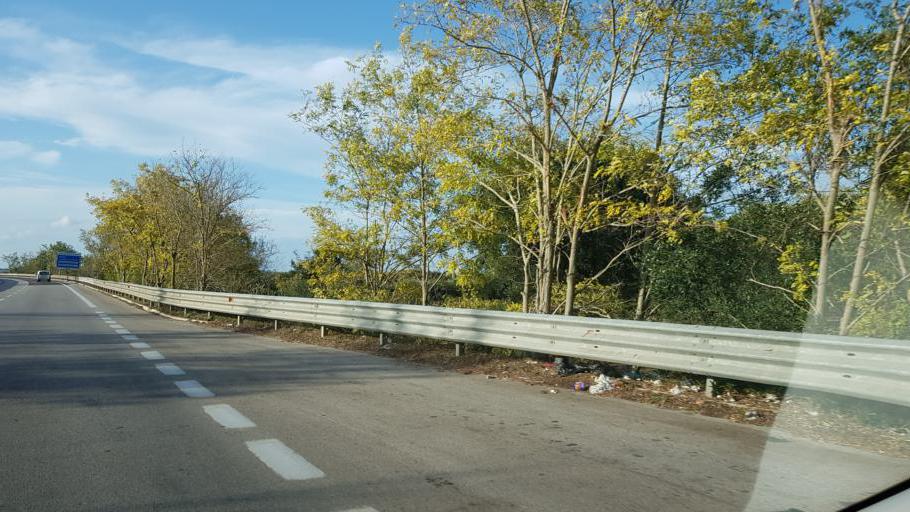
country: IT
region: Apulia
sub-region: Provincia di Brindisi
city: Francavilla Fontana
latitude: 40.5440
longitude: 17.5984
